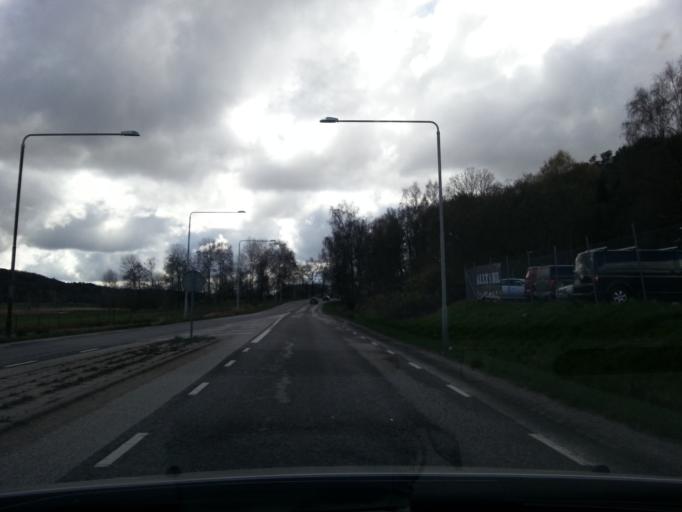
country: SE
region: Vaestra Goetaland
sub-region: Goteborg
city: Goeteborg
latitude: 57.7588
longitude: 11.9392
